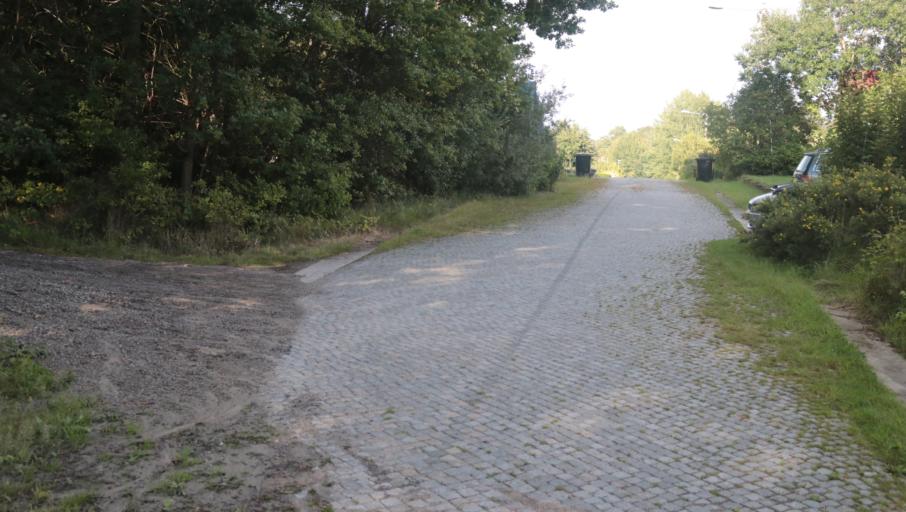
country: SE
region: Blekinge
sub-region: Karlshamns Kommun
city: Karlshamn
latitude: 56.1731
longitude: 14.8988
